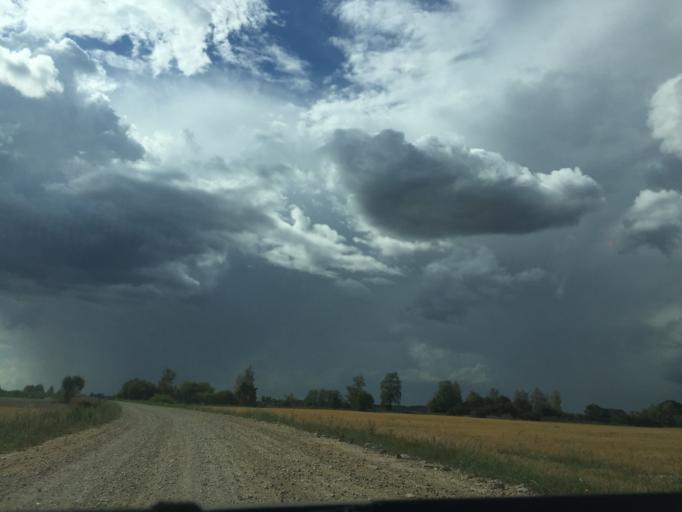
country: LT
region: Siauliu apskritis
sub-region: Joniskis
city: Joniskis
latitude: 56.3741
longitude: 23.5640
